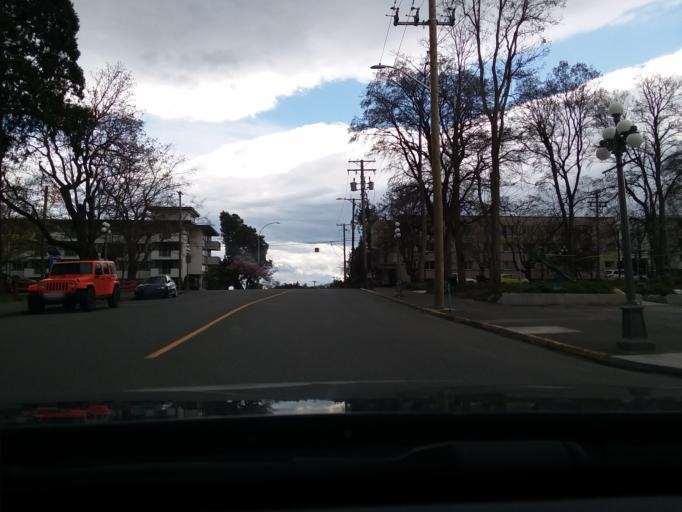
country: CA
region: British Columbia
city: Victoria
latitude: 48.4224
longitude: -123.3602
